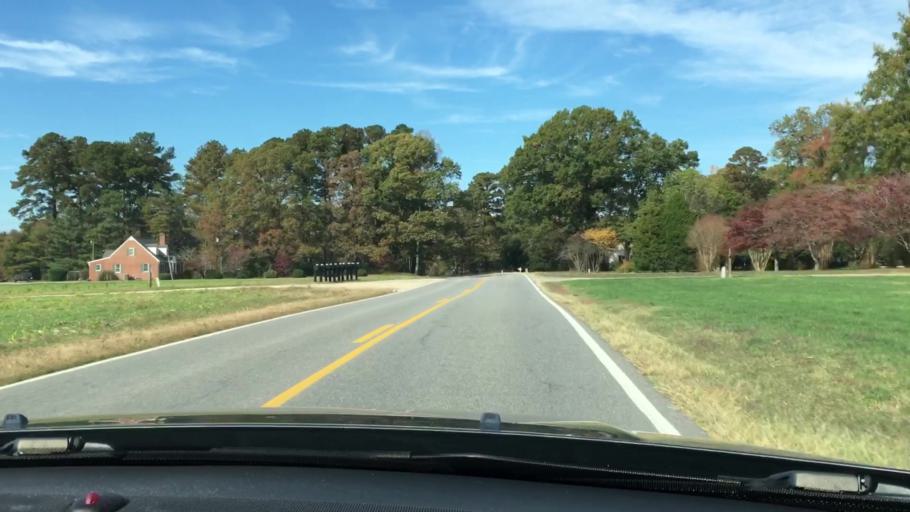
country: US
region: Virginia
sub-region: King William County
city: West Point
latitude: 37.5177
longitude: -76.8219
